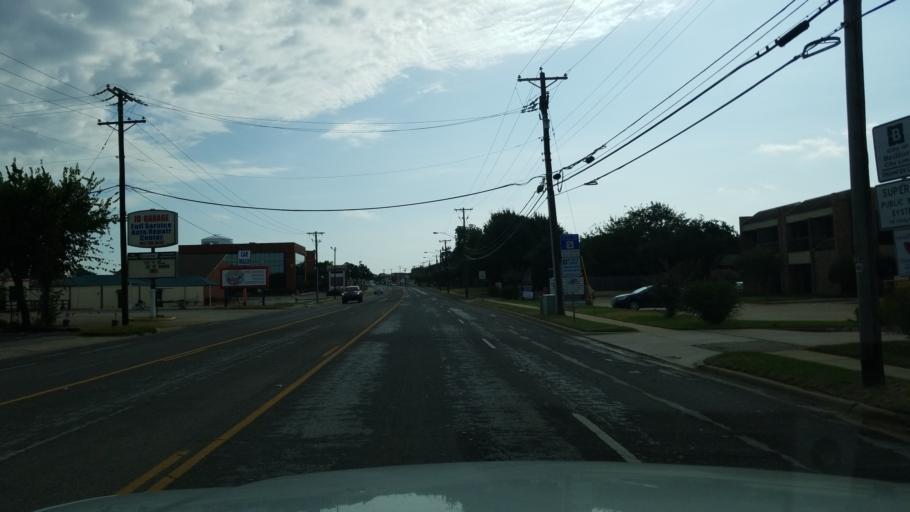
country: US
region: Texas
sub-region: Tarrant County
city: Hurst
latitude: 32.8339
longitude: -97.1666
